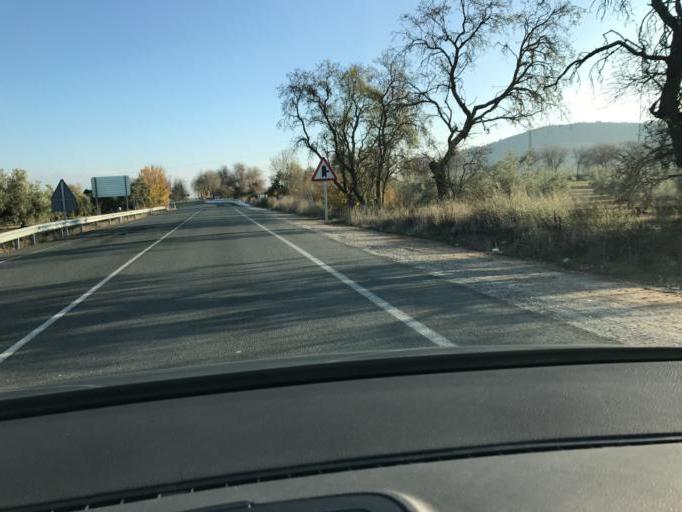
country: ES
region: Andalusia
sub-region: Provincia de Granada
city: Atarfe
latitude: 37.2669
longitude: -3.6802
